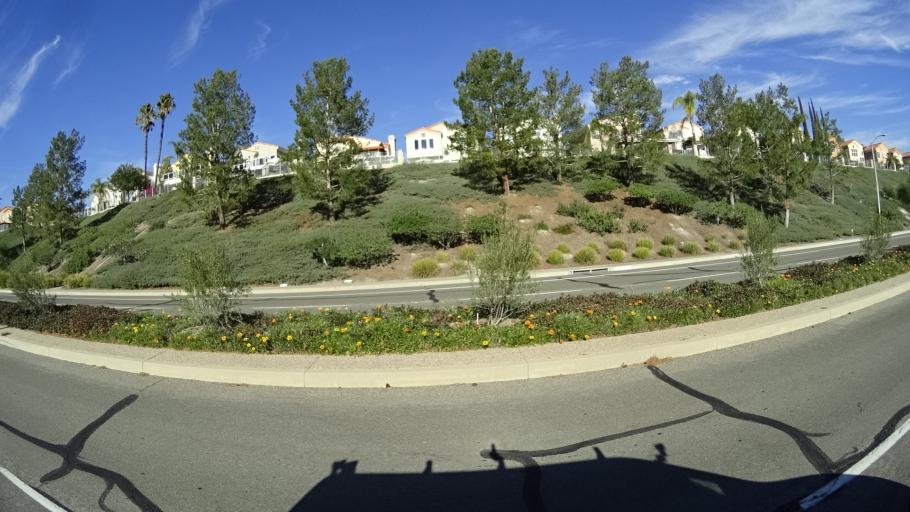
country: US
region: California
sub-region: Orange County
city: Foothill Ranch
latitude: 33.6851
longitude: -117.6695
